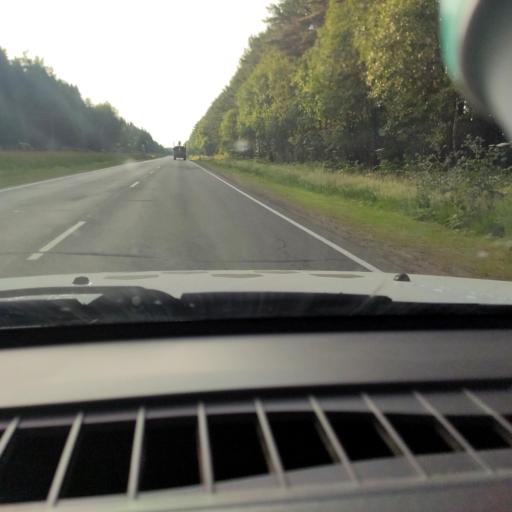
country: RU
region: Kirov
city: Slobodskoy
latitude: 58.7799
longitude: 50.4514
